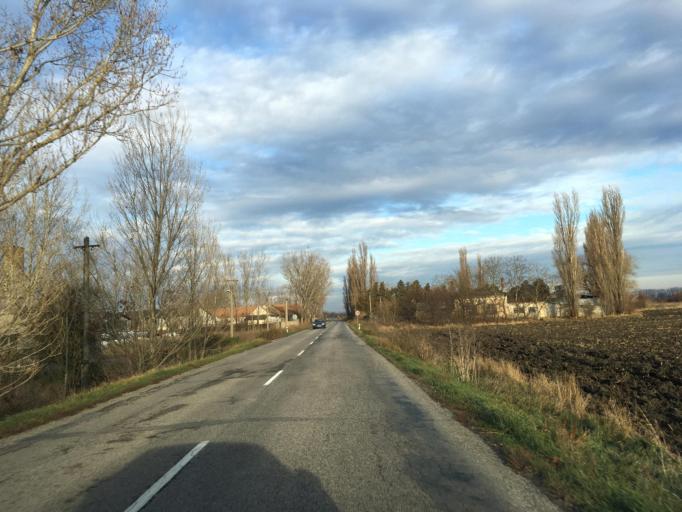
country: SK
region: Trnavsky
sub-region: Okres Dunajska Streda
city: Velky Meder
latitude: 47.8980
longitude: 17.8470
